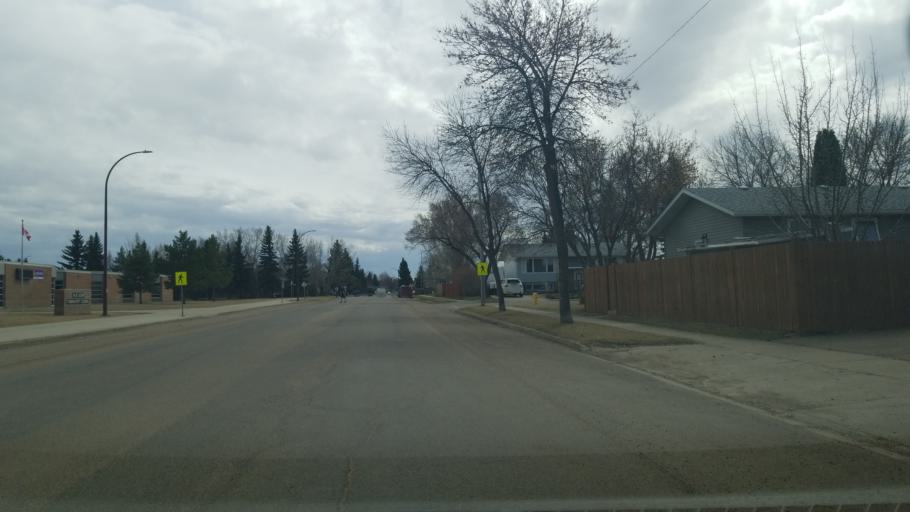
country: CA
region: Saskatchewan
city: Lloydminster
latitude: 53.2721
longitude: -109.9975
